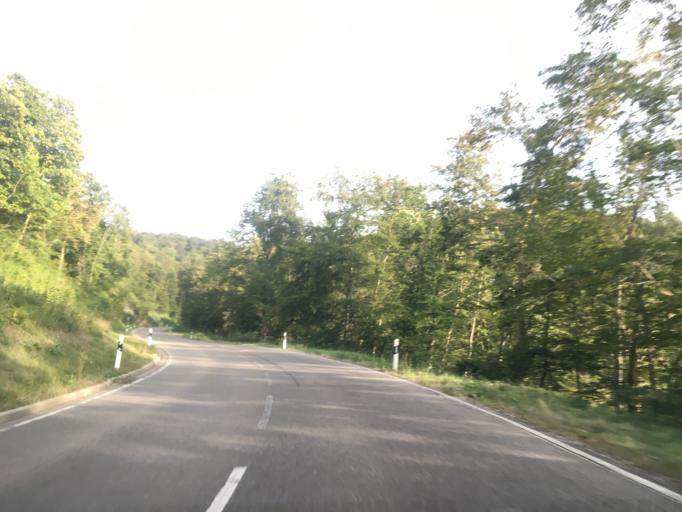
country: DE
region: Baden-Wuerttemberg
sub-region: Tuebingen Region
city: Eningen unter Achalm
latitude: 48.4920
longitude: 9.2893
